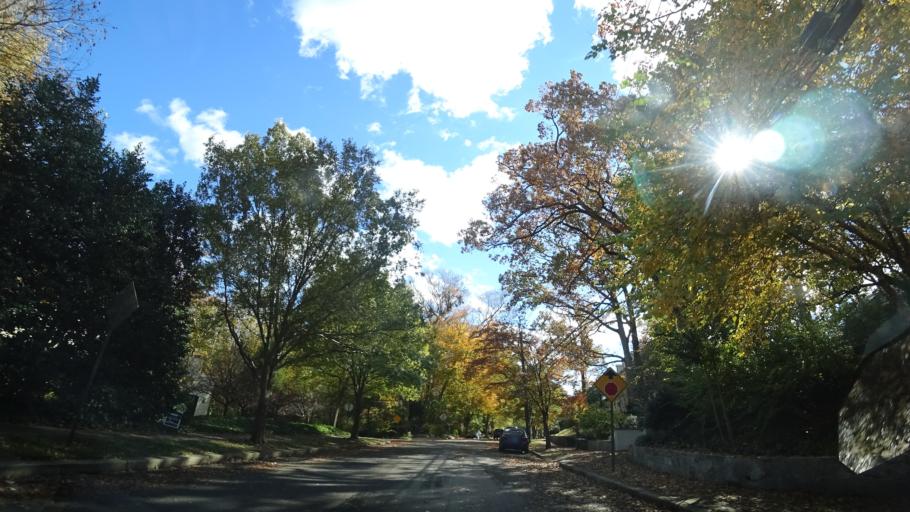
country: US
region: Maryland
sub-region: Montgomery County
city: Chevy Chase
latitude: 38.9508
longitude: -77.0579
